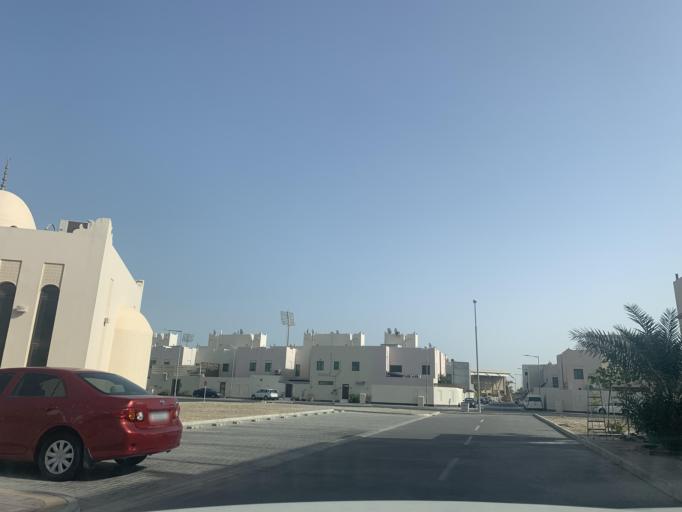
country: BH
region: Northern
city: Sitrah
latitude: 26.1590
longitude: 50.6253
